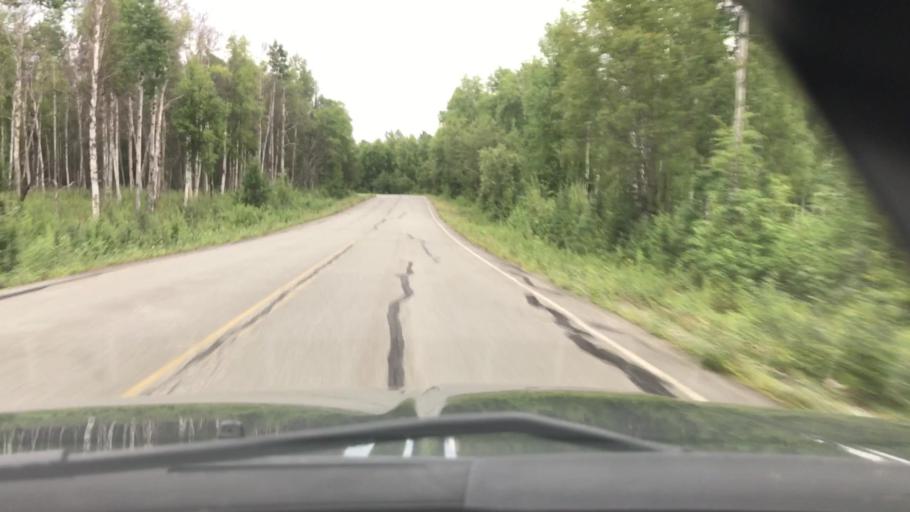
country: US
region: Alaska
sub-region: Matanuska-Susitna Borough
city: Willow
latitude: 61.7639
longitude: -150.1254
